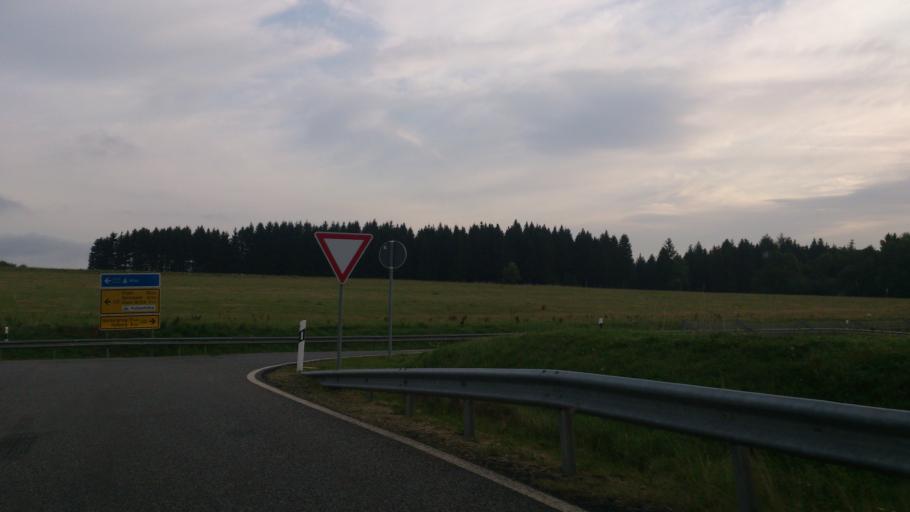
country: DE
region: Rheinland-Pfalz
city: Kradenbach
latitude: 50.2696
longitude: 6.8283
